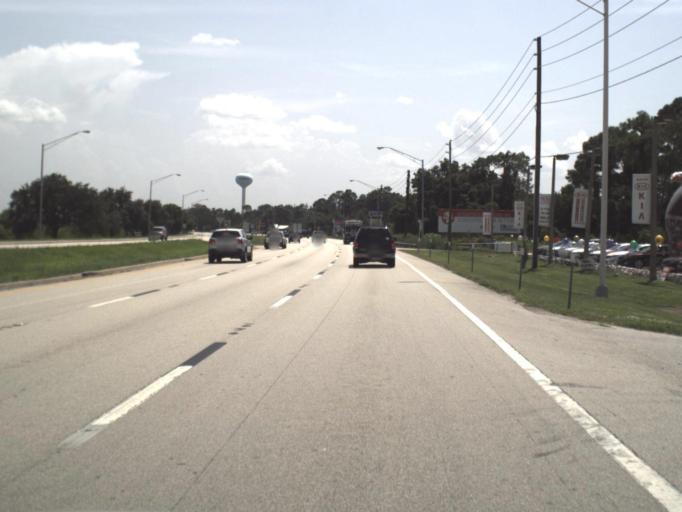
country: US
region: Florida
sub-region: Highlands County
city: Sebring
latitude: 27.4792
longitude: -81.4765
